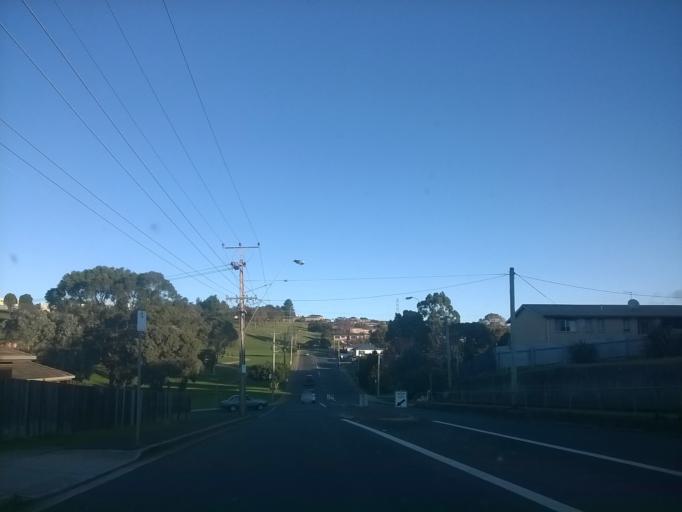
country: AU
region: Tasmania
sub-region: Burnie
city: Burnie
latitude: -41.0763
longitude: 145.8998
